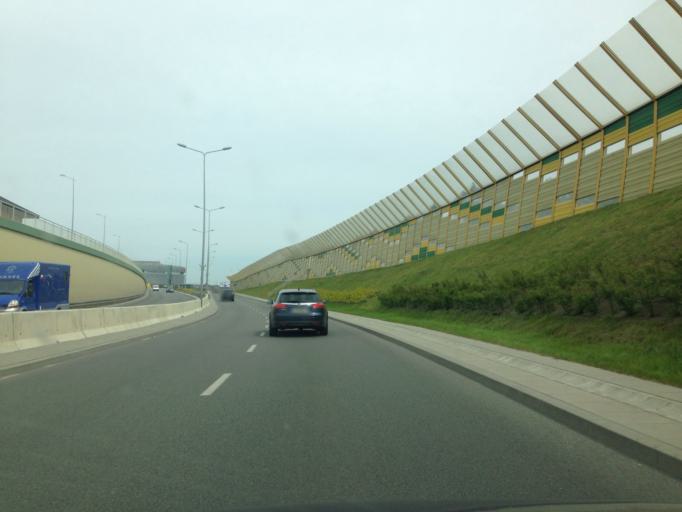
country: PL
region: Pomeranian Voivodeship
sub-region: Sopot
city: Sopot
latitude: 54.4240
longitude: 18.5716
